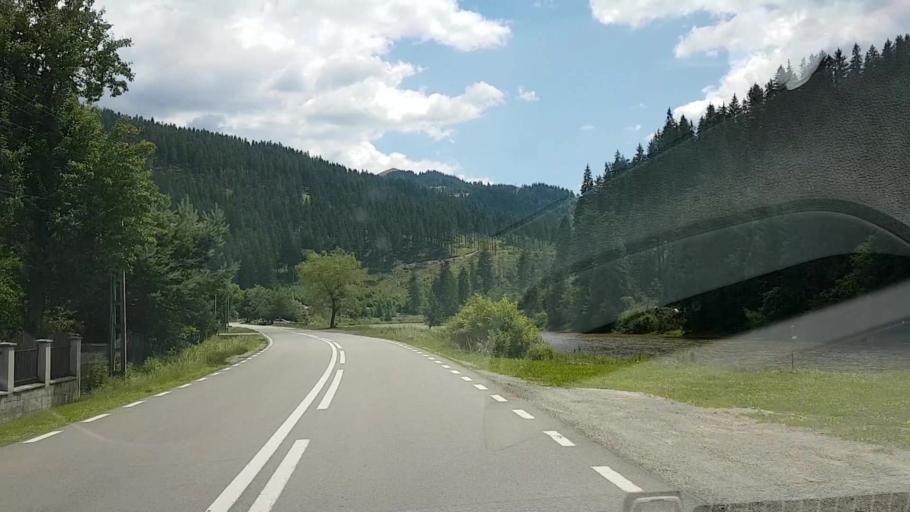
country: RO
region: Suceava
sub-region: Comuna Crucea
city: Crucea
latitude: 47.3580
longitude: 25.6101
